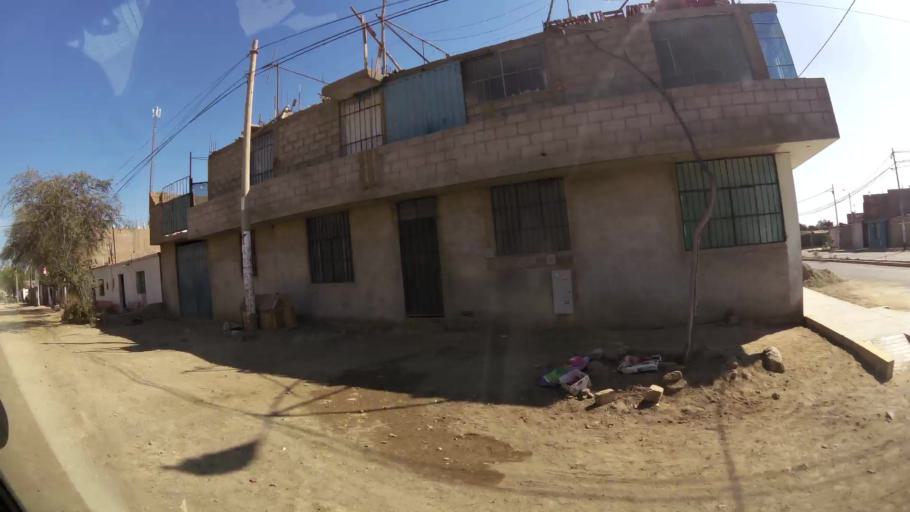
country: PE
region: Ica
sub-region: Provincia de Ica
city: La Tinguina
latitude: -14.0372
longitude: -75.7042
